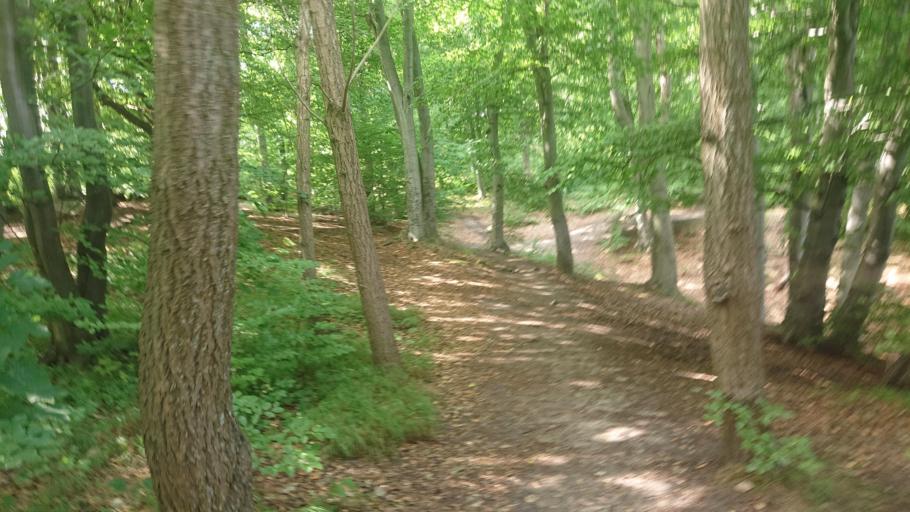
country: PL
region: Pomeranian Voivodeship
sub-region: Sopot
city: Sopot
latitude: 54.4684
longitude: 18.5618
